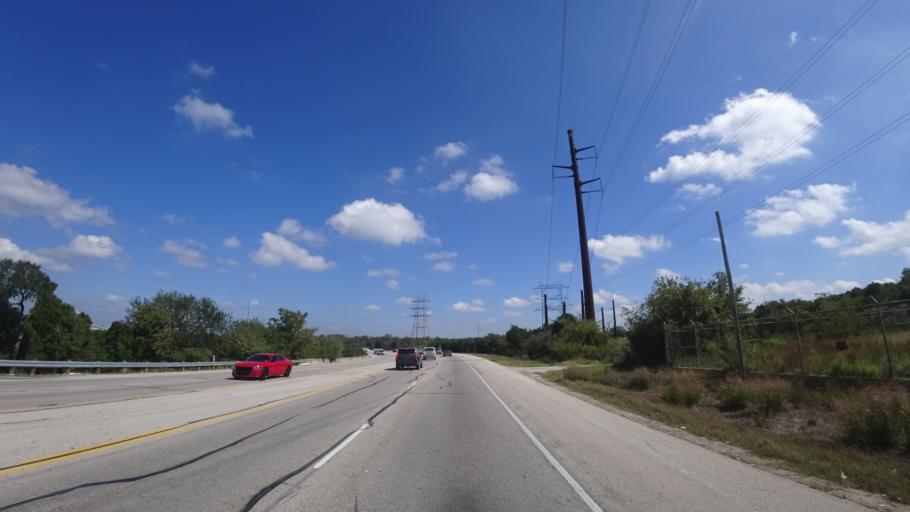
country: US
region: Texas
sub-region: Travis County
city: Hudson Bend
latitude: 30.3966
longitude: -97.8594
